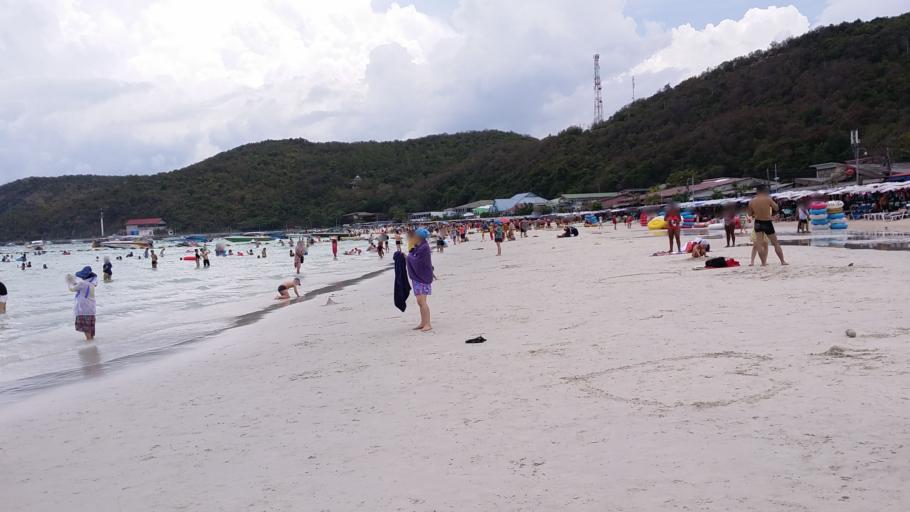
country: TH
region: Chon Buri
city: Ban Ko Lan
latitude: 12.9249
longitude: 100.7759
